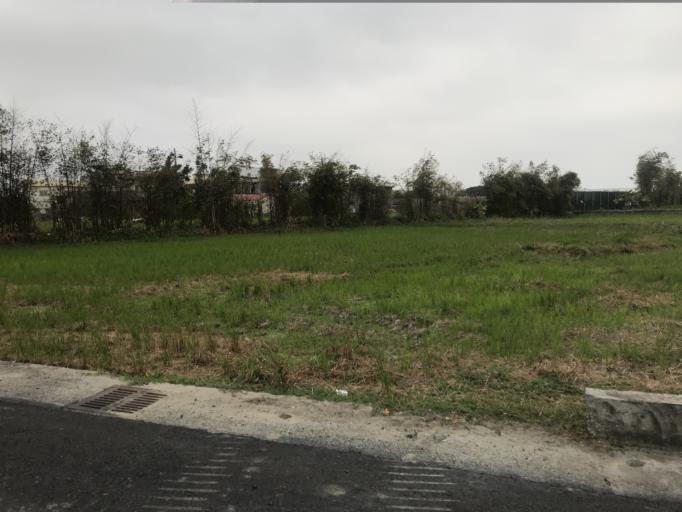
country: TW
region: Taiwan
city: Fengyuan
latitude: 24.3685
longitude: 120.6019
